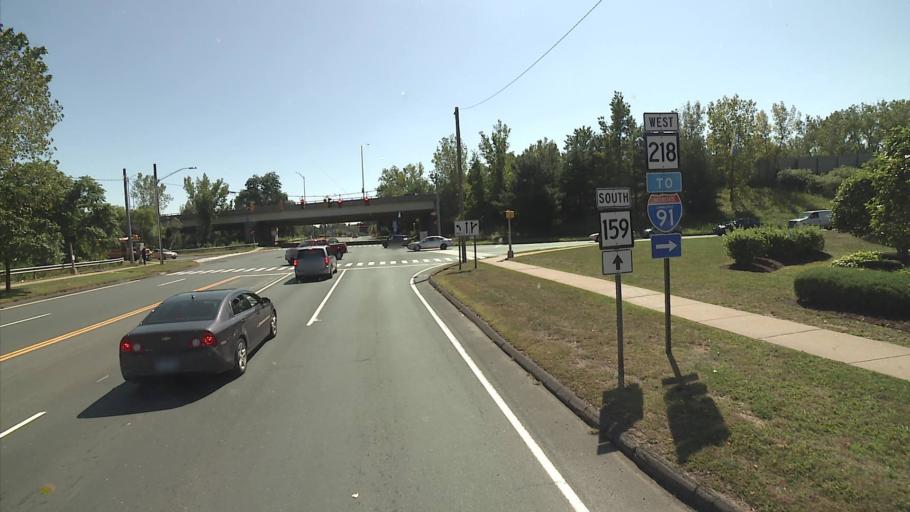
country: US
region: Connecticut
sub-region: Hartford County
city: South Windsor
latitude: 41.8190
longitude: -72.6569
